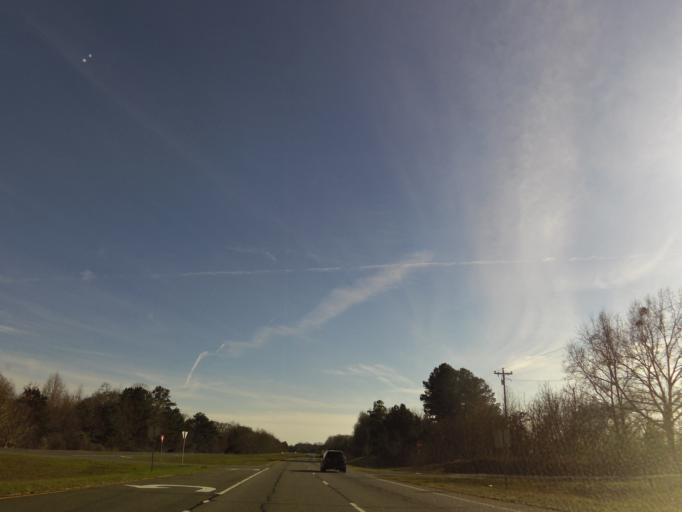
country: US
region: Georgia
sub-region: Chattahoochee County
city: Cusseta
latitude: 32.2301
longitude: -84.7125
